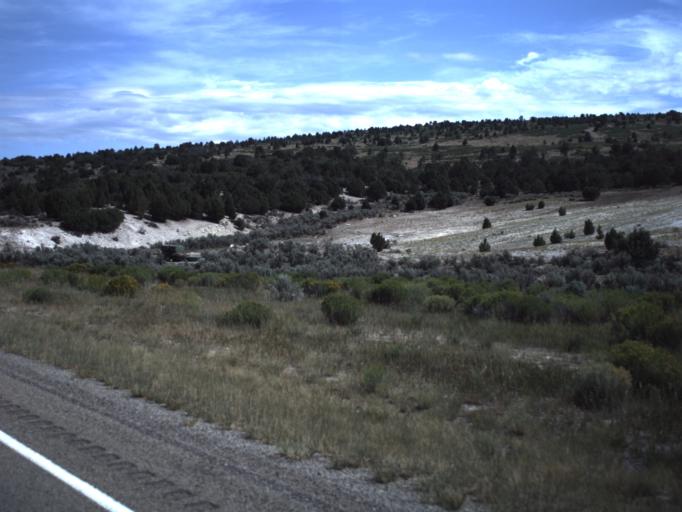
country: US
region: Utah
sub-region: Sanpete County
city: Fairview
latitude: 39.7170
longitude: -111.4709
